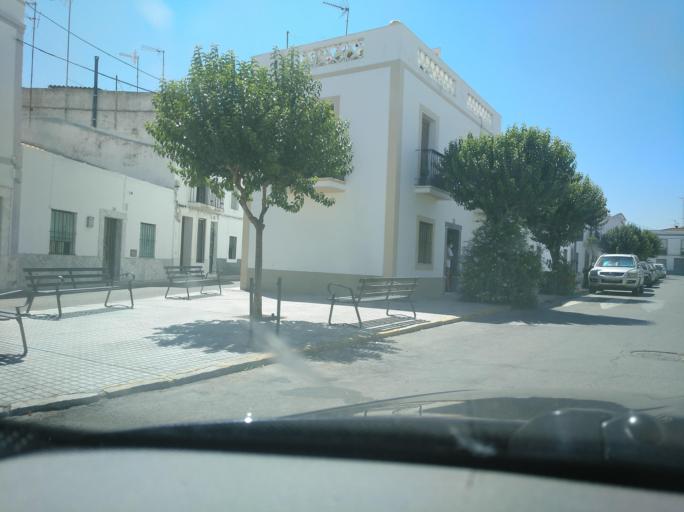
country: ES
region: Extremadura
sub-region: Provincia de Badajoz
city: Olivenza
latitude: 38.6869
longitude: -7.1021
